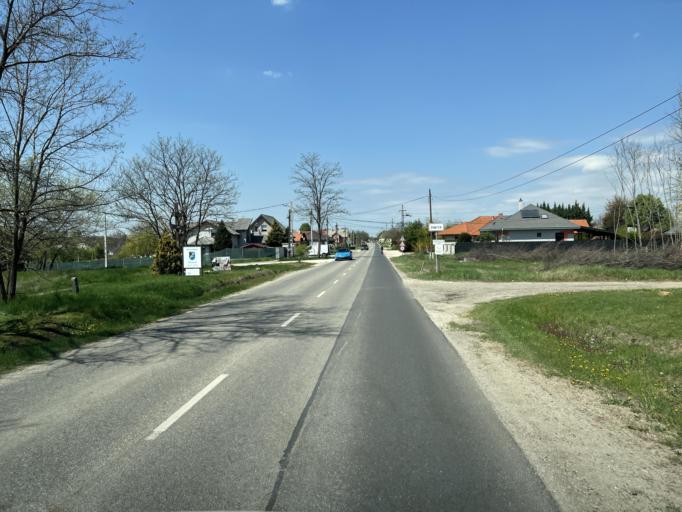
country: HU
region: Pest
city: Inarcs
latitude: 47.2496
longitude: 19.3371
